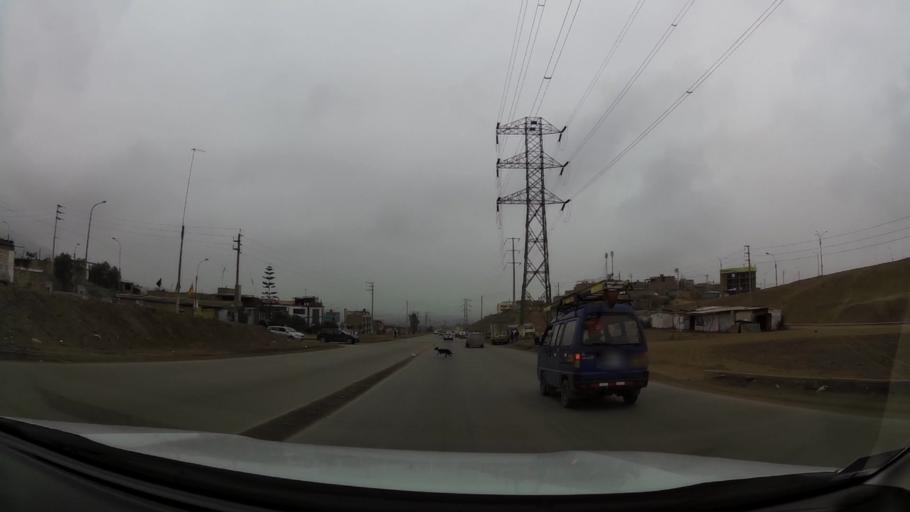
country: PE
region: Lima
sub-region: Lima
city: Surco
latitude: -12.2267
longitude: -76.9167
